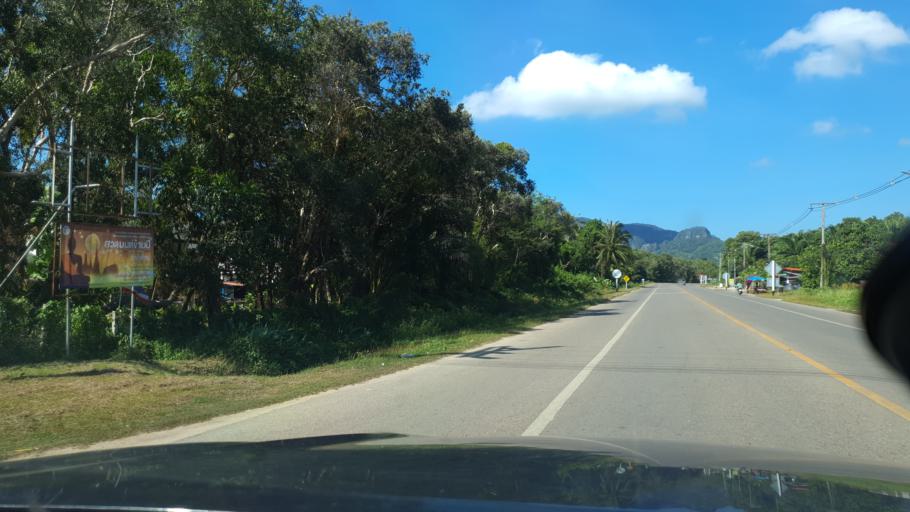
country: TH
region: Krabi
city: Krabi
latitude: 8.0266
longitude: 98.8779
